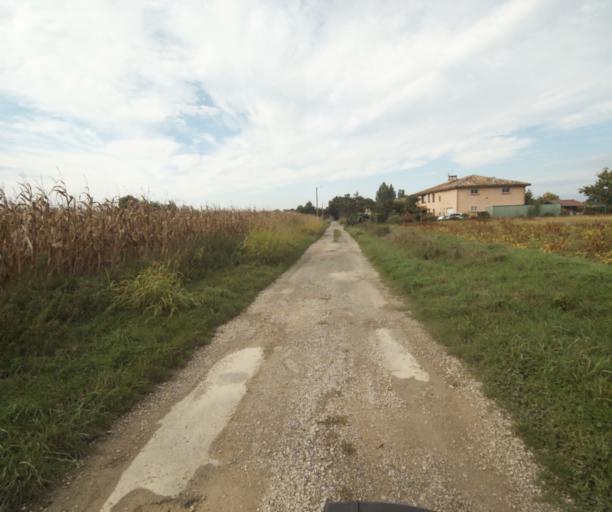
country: FR
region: Midi-Pyrenees
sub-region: Departement du Tarn-et-Garonne
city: Finhan
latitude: 43.9201
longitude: 1.2338
